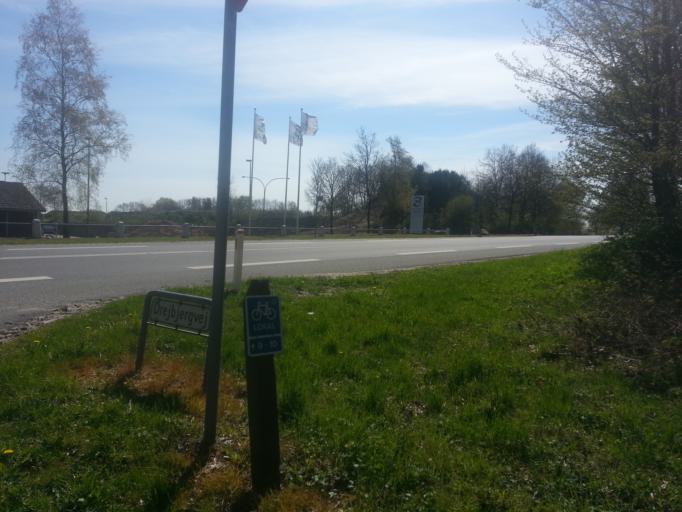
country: DK
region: South Denmark
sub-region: Aabenraa Kommune
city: Aabenraa
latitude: 54.9554
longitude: 9.4489
